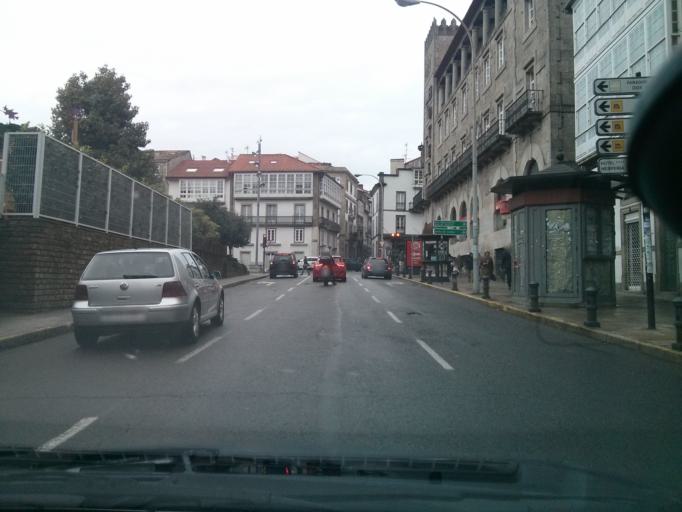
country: ES
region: Galicia
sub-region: Provincia da Coruna
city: Santiago de Compostela
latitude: 42.8761
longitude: -8.5440
